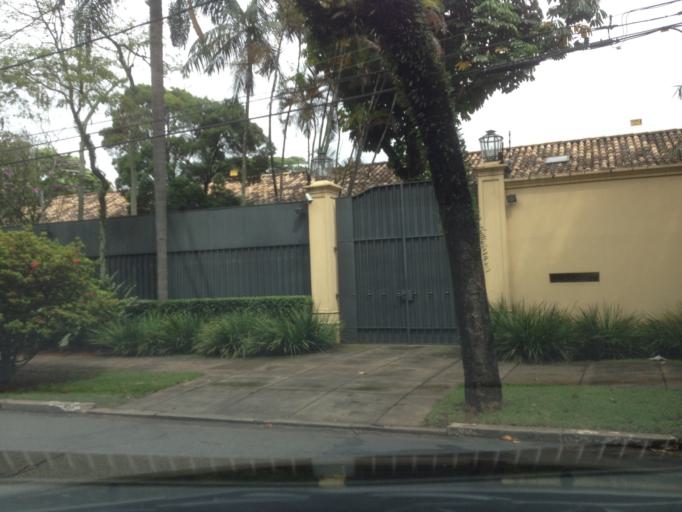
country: BR
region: Sao Paulo
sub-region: Sao Paulo
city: Sao Paulo
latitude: -23.5672
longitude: -46.6752
